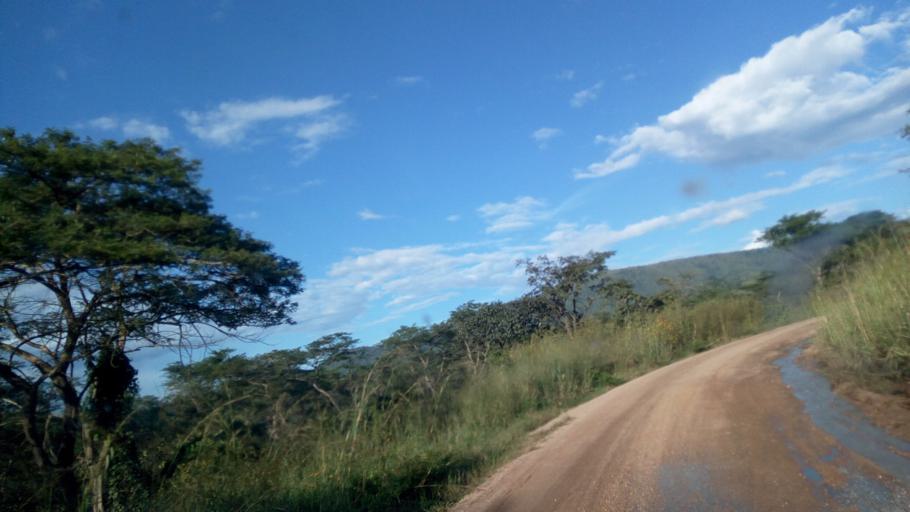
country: TZ
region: Kigoma
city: Kigoma
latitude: -4.6557
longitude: 28.7555
